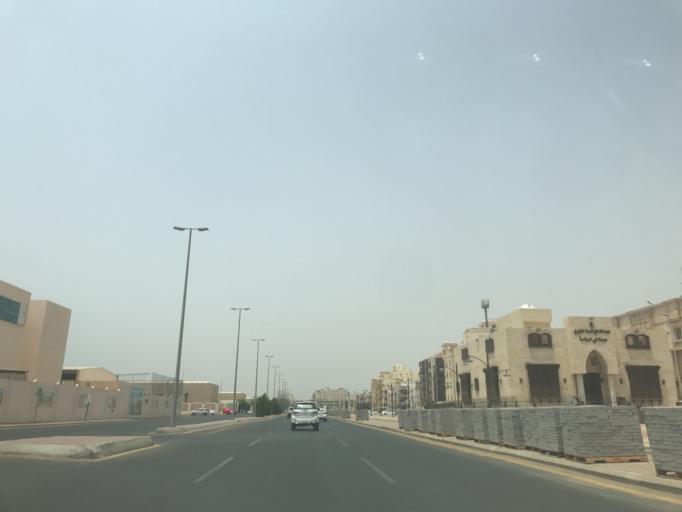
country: SA
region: Makkah
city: Jeddah
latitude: 21.5869
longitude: 39.1480
